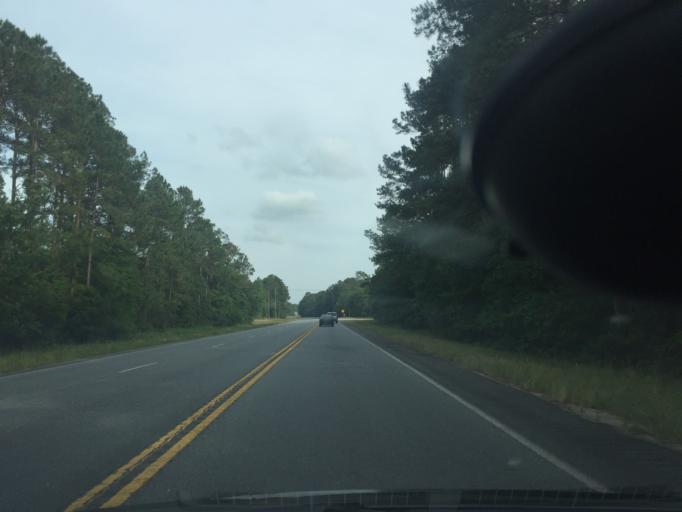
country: US
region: Georgia
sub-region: Chatham County
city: Bloomingdale
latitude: 32.0481
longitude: -81.3381
